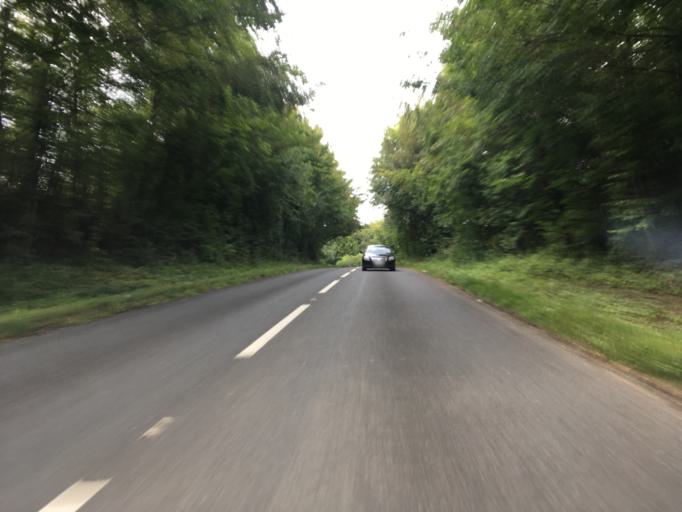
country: GB
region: England
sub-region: Hampshire
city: Overton
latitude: 51.1917
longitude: -1.2556
